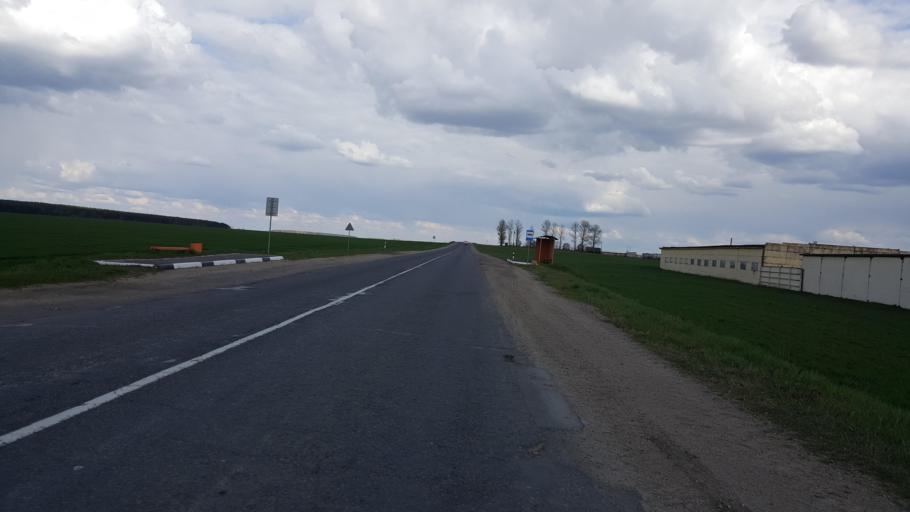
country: BY
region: Brest
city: Kamyanyets
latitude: 52.4169
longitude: 23.6209
